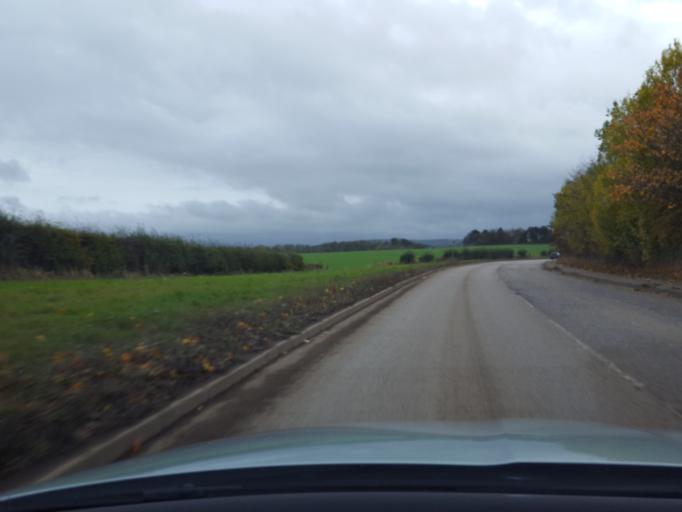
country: GB
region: Scotland
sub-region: Edinburgh
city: Newbridge
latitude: 55.9148
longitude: -3.3981
